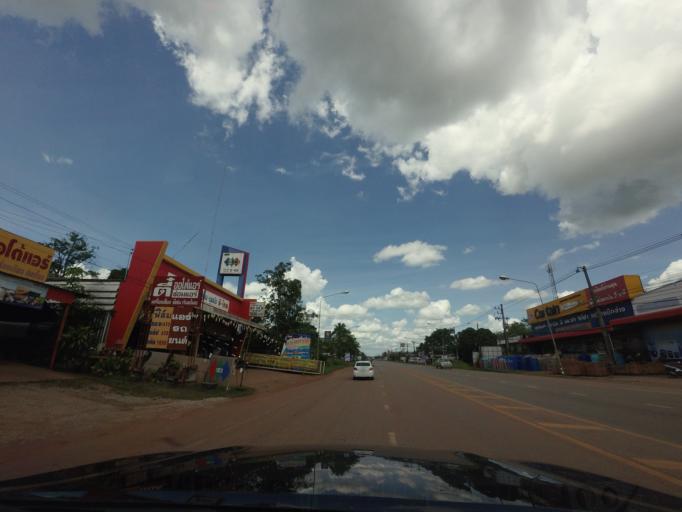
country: TH
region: Changwat Udon Thani
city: Ban Dung
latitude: 17.6797
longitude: 103.2545
